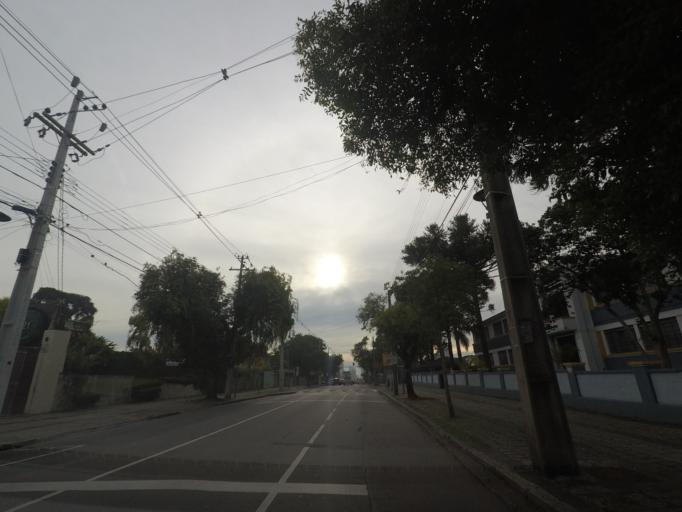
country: BR
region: Parana
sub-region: Curitiba
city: Curitiba
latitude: -25.4393
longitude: -49.2923
